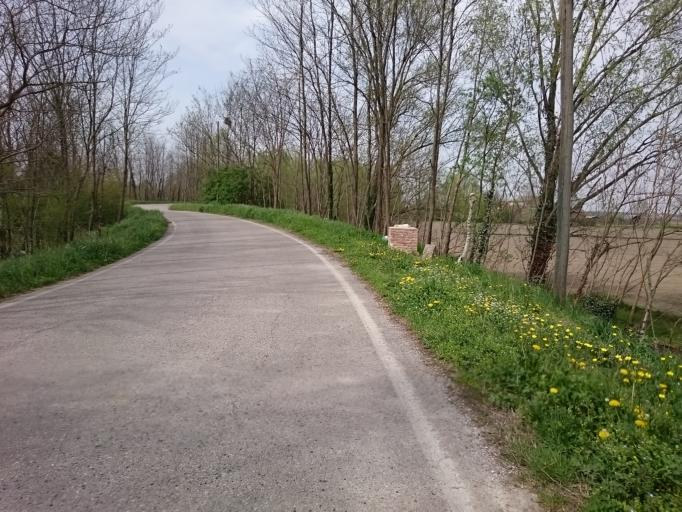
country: IT
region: Veneto
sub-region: Provincia di Padova
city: Anguillara Veneta
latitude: 45.1531
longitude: 11.8595
